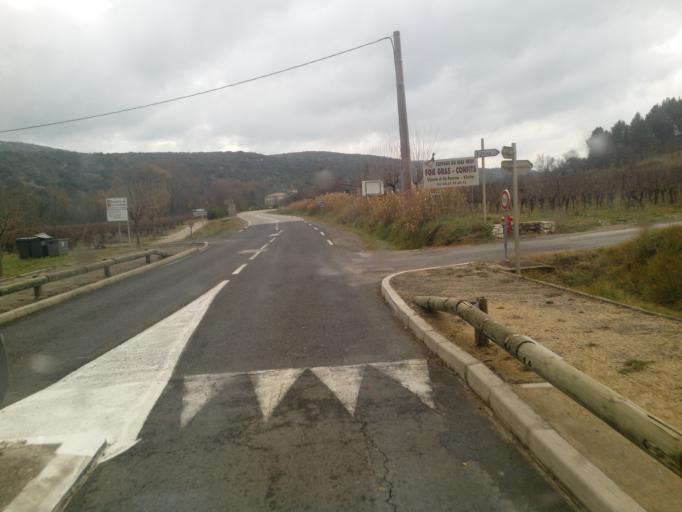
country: FR
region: Languedoc-Roussillon
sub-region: Departement de l'Herault
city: Saint-Bauzille-de-Putois
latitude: 43.9265
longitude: 3.7933
